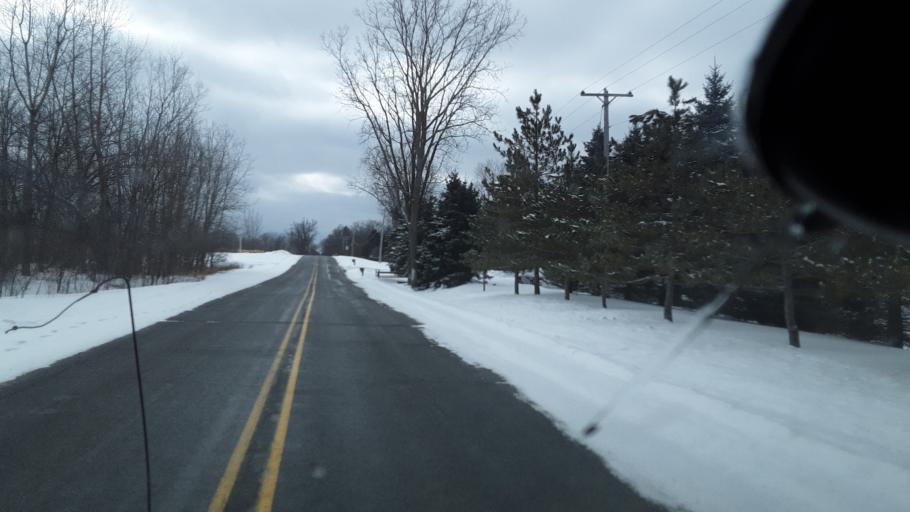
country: US
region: Michigan
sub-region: Eaton County
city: Dimondale
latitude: 42.6373
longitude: -84.5825
